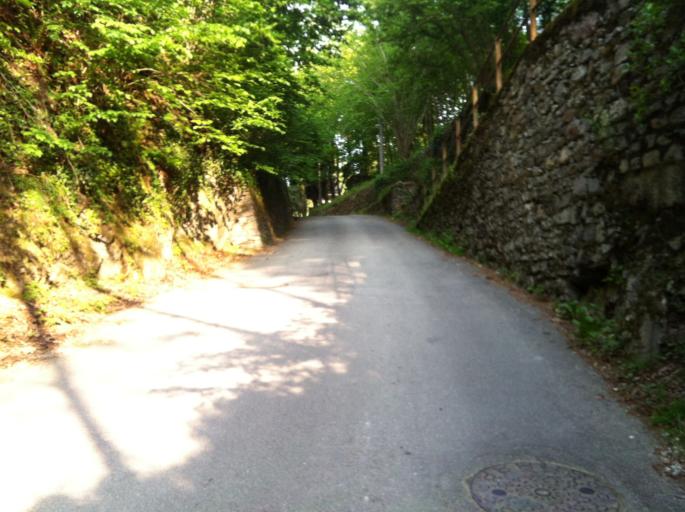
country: IT
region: Lombardy
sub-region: Provincia di Como
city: Grandola ed Uniti
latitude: 46.0280
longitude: 9.2253
